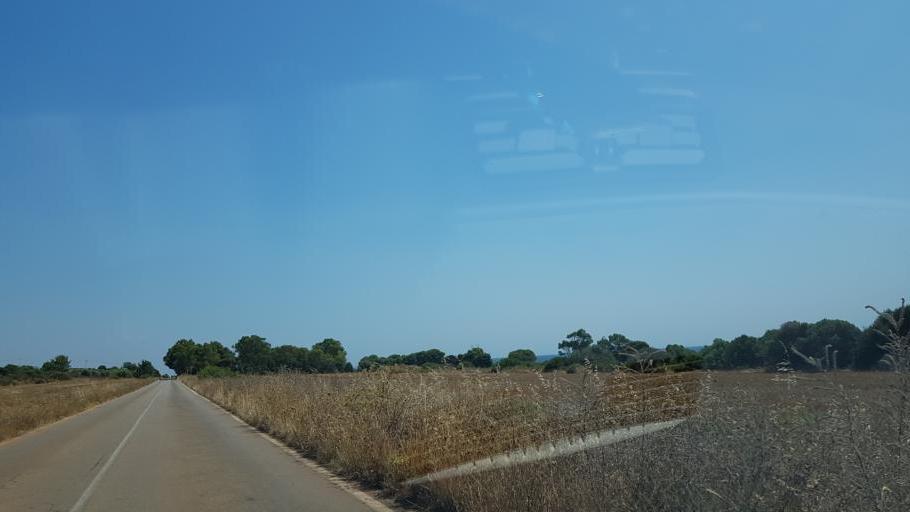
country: IT
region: Apulia
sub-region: Provincia di Lecce
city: Nardo
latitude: 40.1822
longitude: 17.9383
